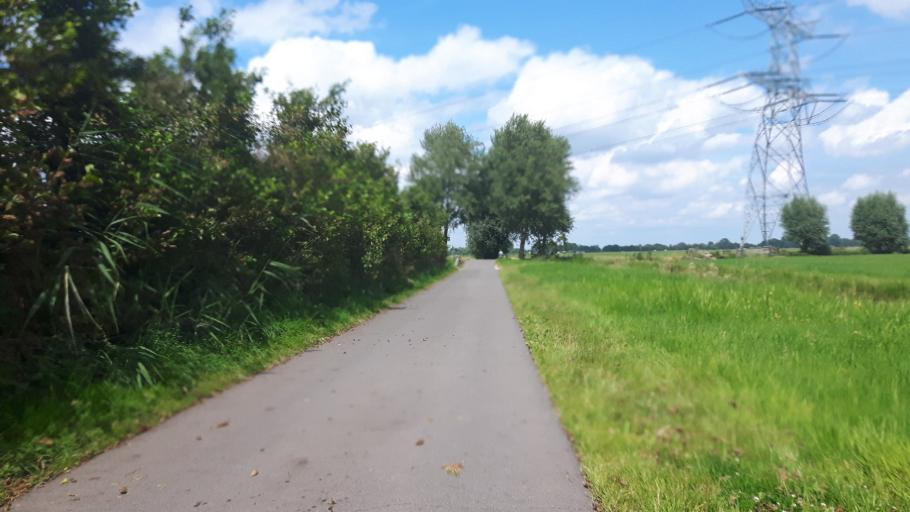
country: NL
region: South Holland
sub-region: Molenwaard
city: Nieuw-Lekkerland
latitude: 51.9052
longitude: 4.6582
